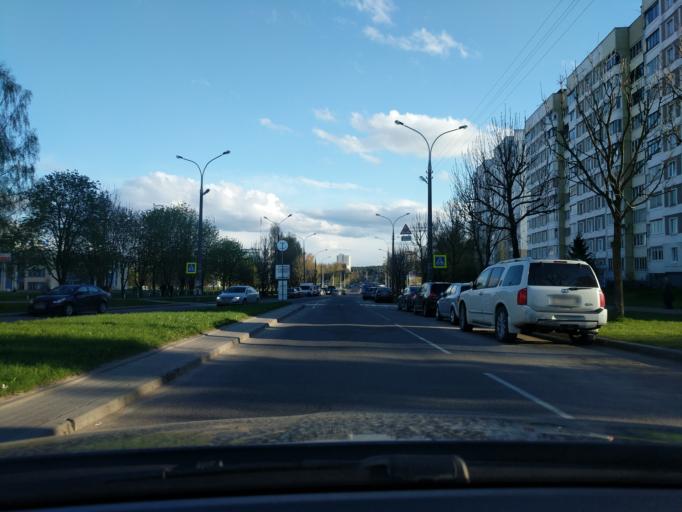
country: BY
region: Minsk
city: Novoye Medvezhino
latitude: 53.9011
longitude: 27.4530
